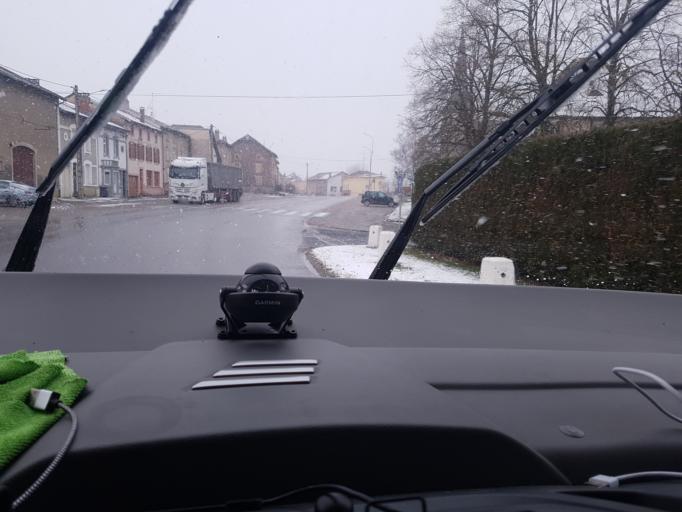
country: FR
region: Lorraine
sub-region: Departement de Meurthe-et-Moselle
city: Baccarat
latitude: 48.5616
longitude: 6.8074
